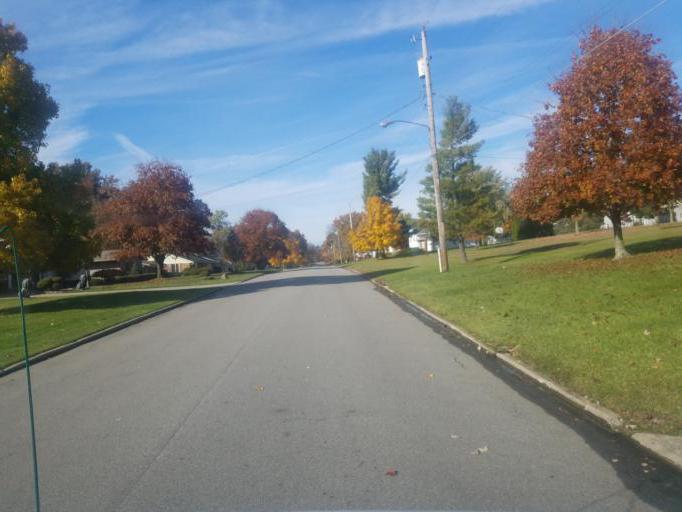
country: US
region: Ohio
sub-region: Richland County
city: Mansfield
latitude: 40.7262
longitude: -82.5155
